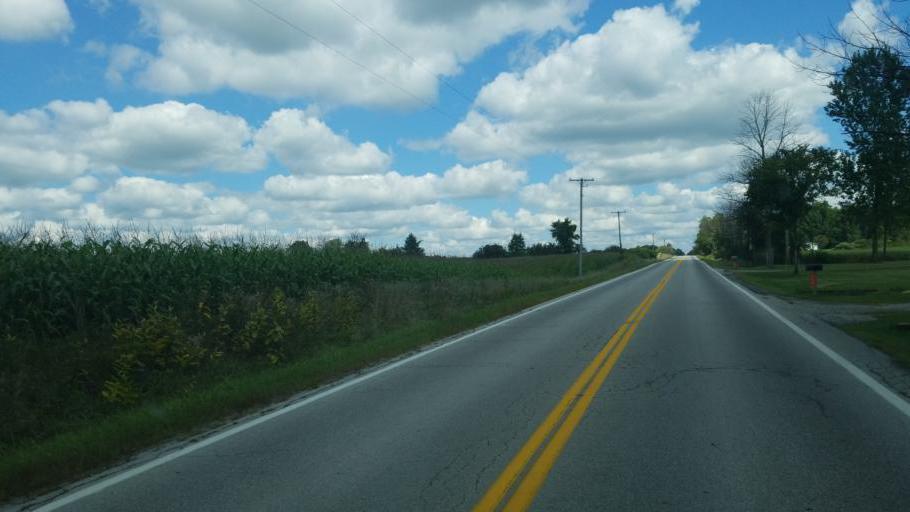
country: US
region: Ohio
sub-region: Wayne County
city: West Salem
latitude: 40.9821
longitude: -82.2335
